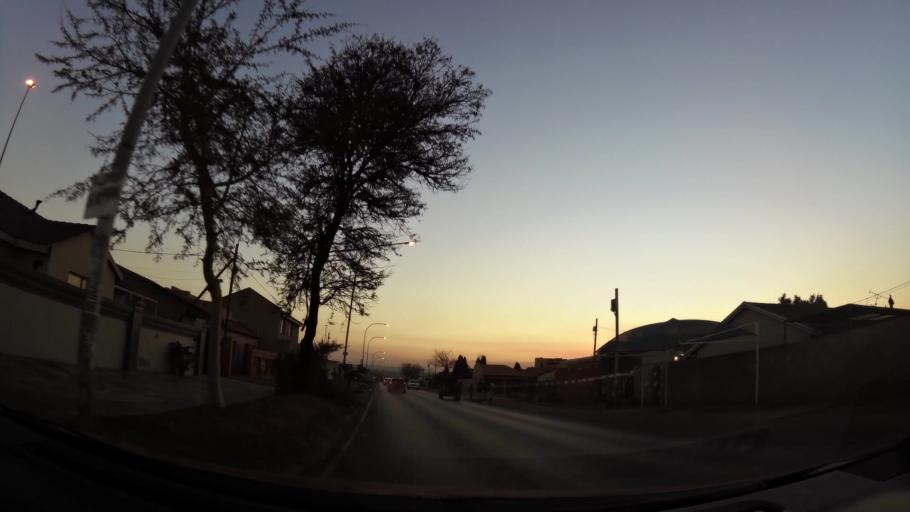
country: ZA
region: Gauteng
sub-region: City of Johannesburg Metropolitan Municipality
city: Soweto
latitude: -26.2342
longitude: 27.8286
